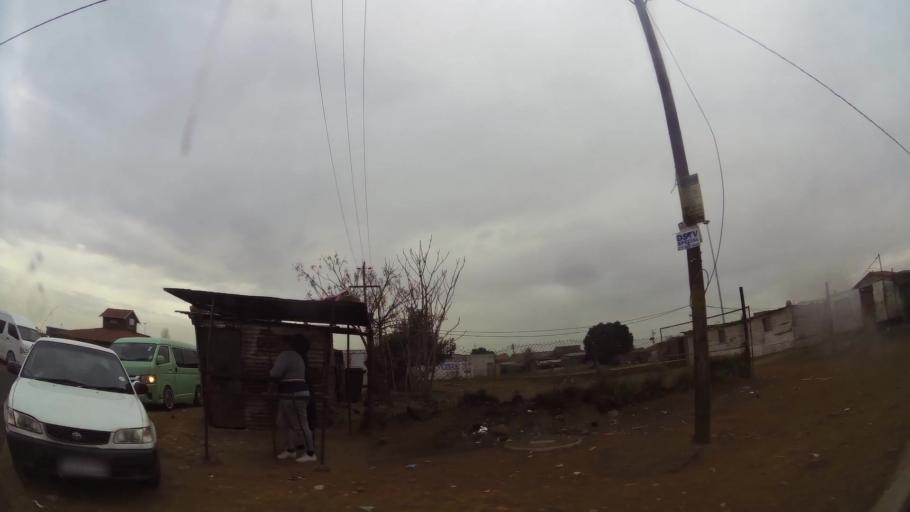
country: ZA
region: Gauteng
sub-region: Ekurhuleni Metropolitan Municipality
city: Germiston
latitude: -26.3847
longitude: 28.1770
